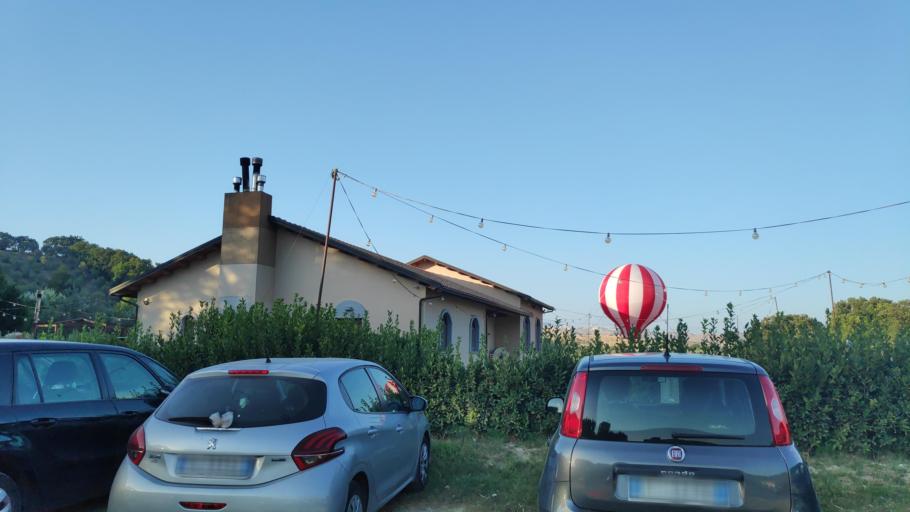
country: IT
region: Calabria
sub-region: Provincia di Catanzaro
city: San Floro
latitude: 38.8503
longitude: 16.5322
